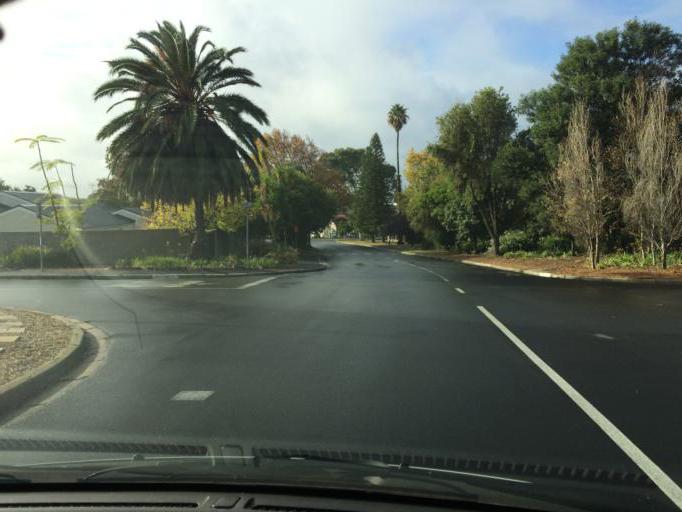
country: ZA
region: Western Cape
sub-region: City of Cape Town
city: Kraaifontein
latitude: -33.8649
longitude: 18.6499
